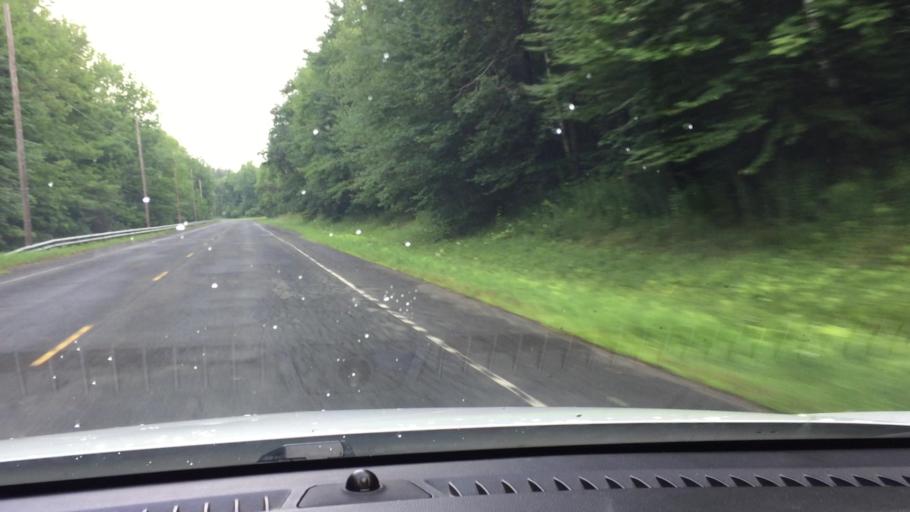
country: US
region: Massachusetts
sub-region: Berkshire County
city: Hinsdale
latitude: 42.4278
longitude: -73.0067
